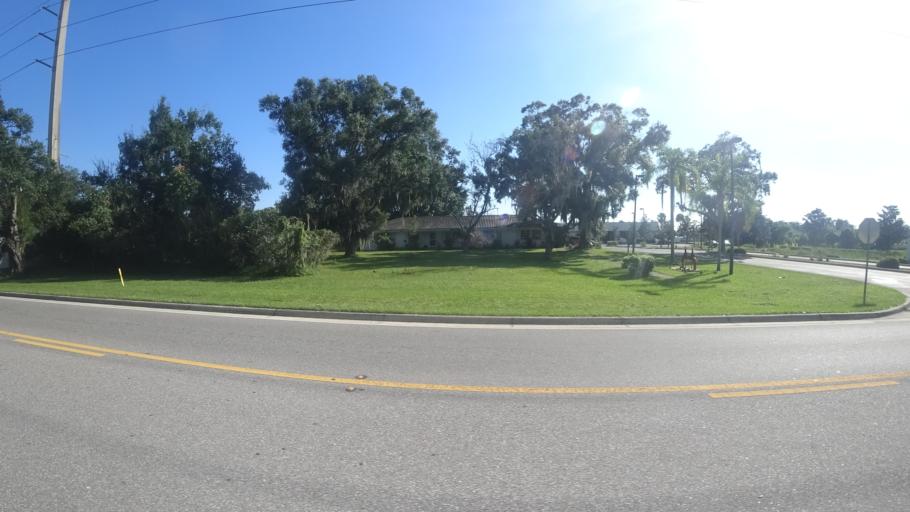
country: US
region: Florida
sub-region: Manatee County
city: West Samoset
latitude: 27.4624
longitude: -82.5601
